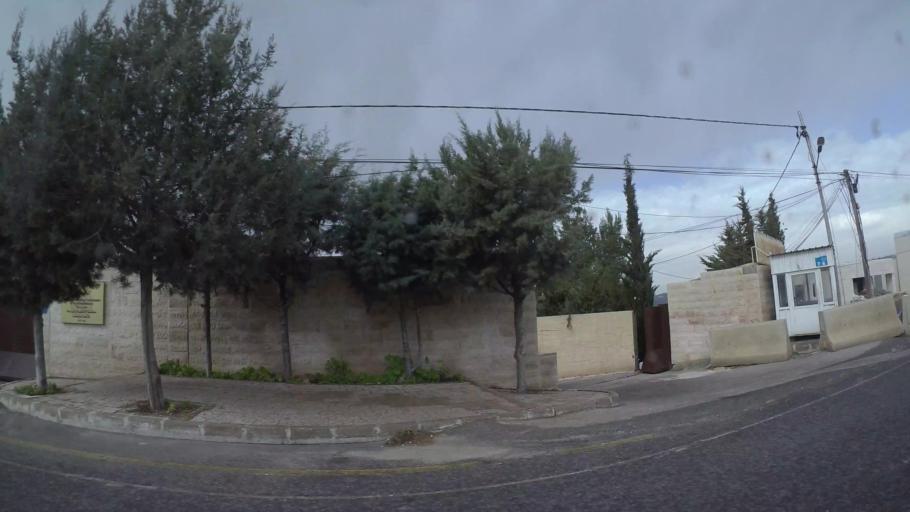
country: JO
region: Amman
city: Wadi as Sir
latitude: 31.9819
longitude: 35.8216
